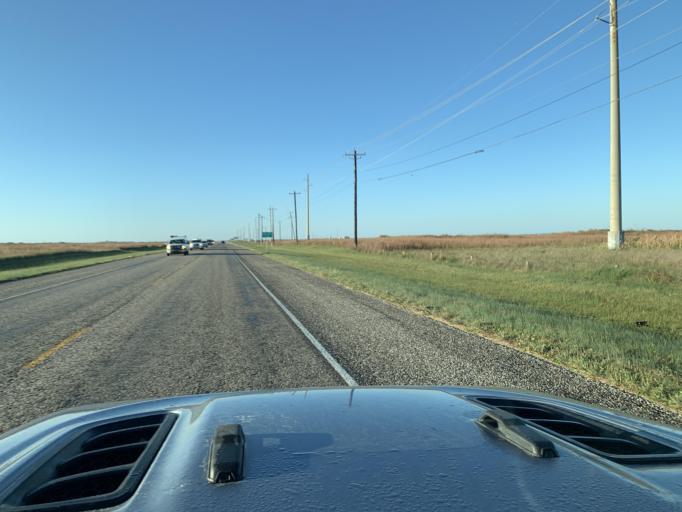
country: US
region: Texas
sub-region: Nueces County
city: Port Aransas
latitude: 27.6551
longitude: -97.1885
